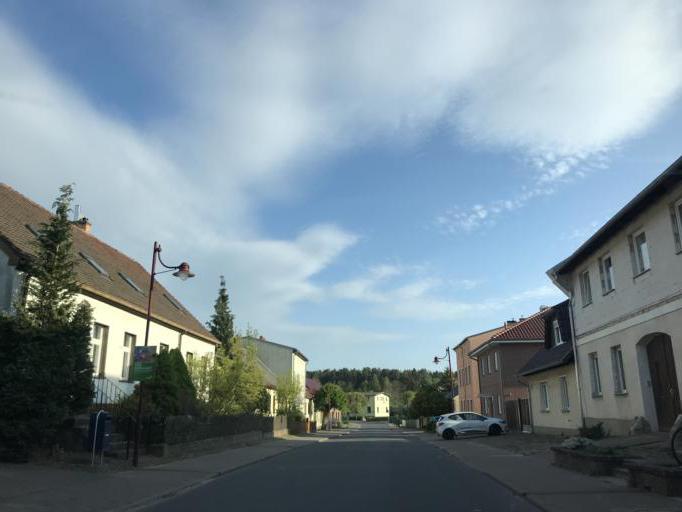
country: DE
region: Brandenburg
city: Joachimsthal
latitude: 52.9742
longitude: 13.7416
